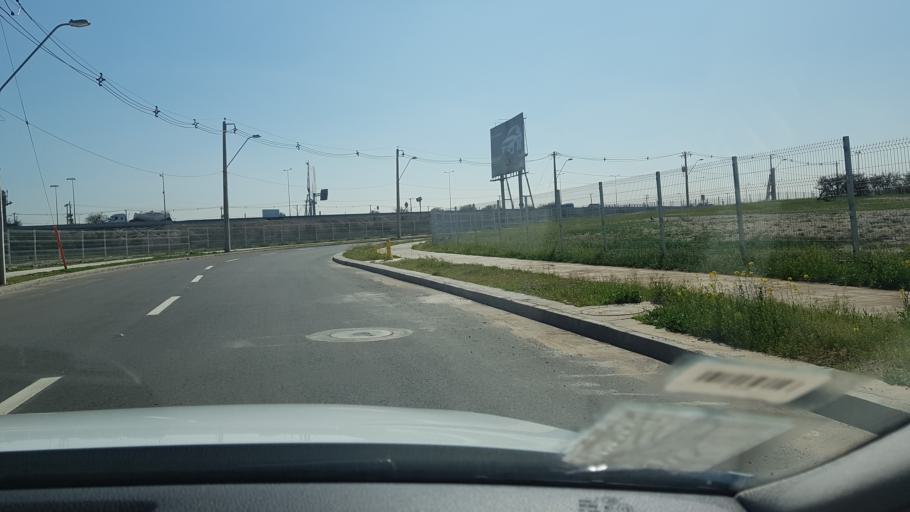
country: CL
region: Santiago Metropolitan
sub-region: Provincia de Santiago
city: Lo Prado
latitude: -33.4192
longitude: -70.7900
